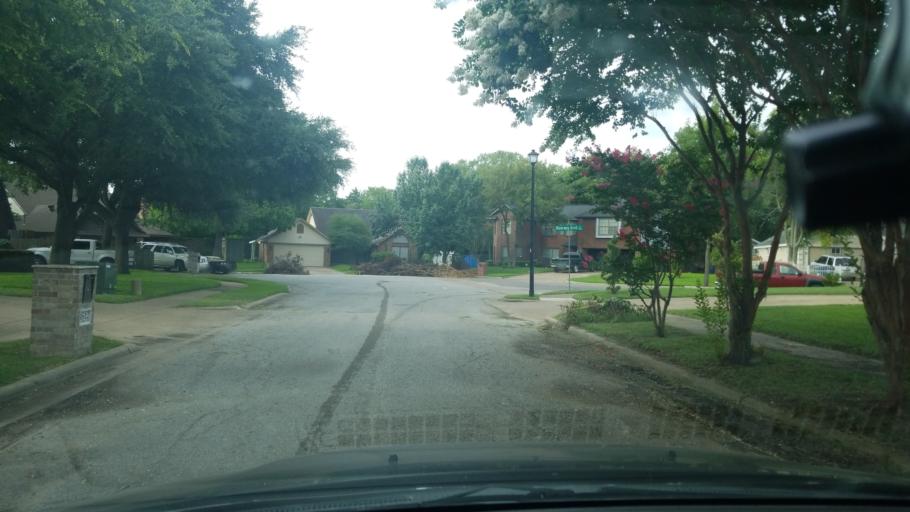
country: US
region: Texas
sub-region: Dallas County
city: Balch Springs
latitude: 32.7390
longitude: -96.6641
